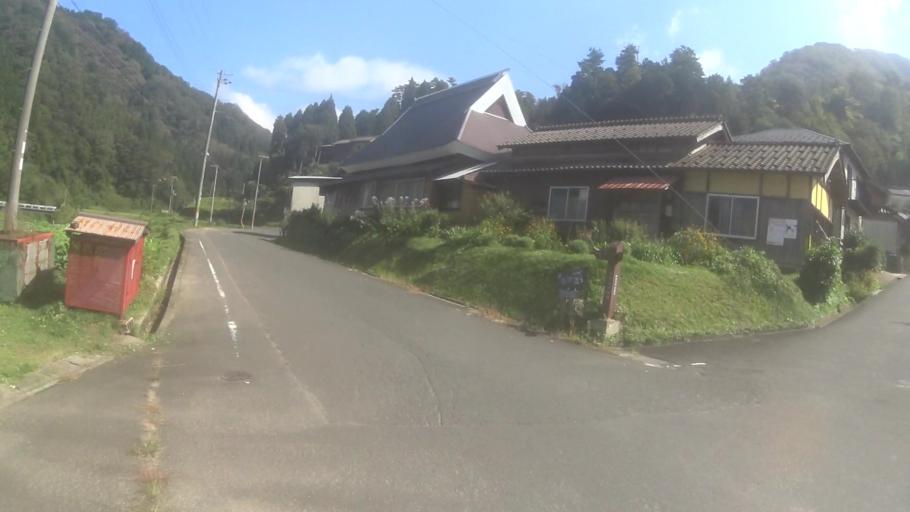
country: JP
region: Kyoto
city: Miyazu
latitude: 35.6795
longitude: 135.1606
